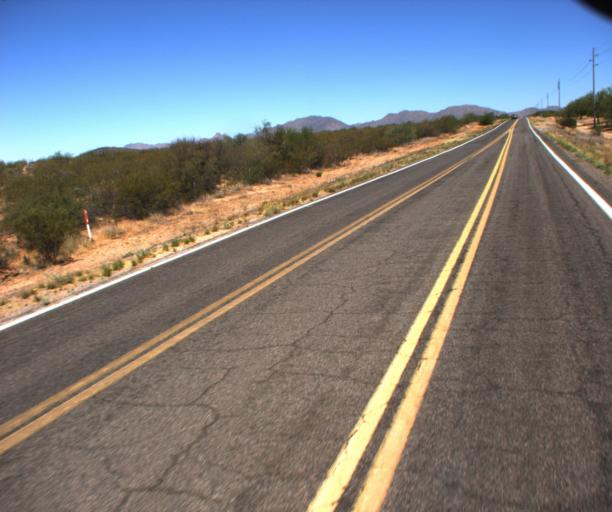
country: US
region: Arizona
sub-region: Yavapai County
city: Congress
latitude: 34.1056
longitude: -112.8316
